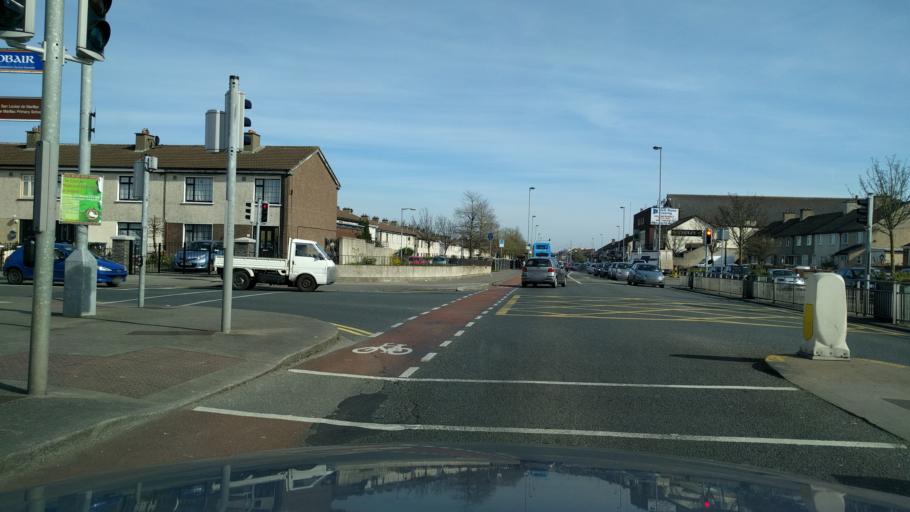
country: IE
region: Leinster
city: Ballyfermot
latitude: 53.3429
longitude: -6.3608
